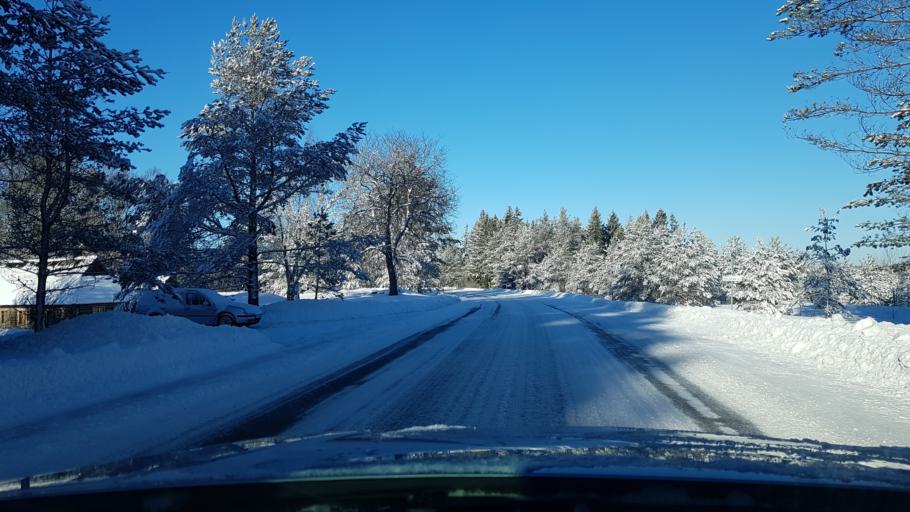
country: EE
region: Hiiumaa
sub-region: Kaerdla linn
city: Kardla
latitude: 58.9352
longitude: 22.7821
